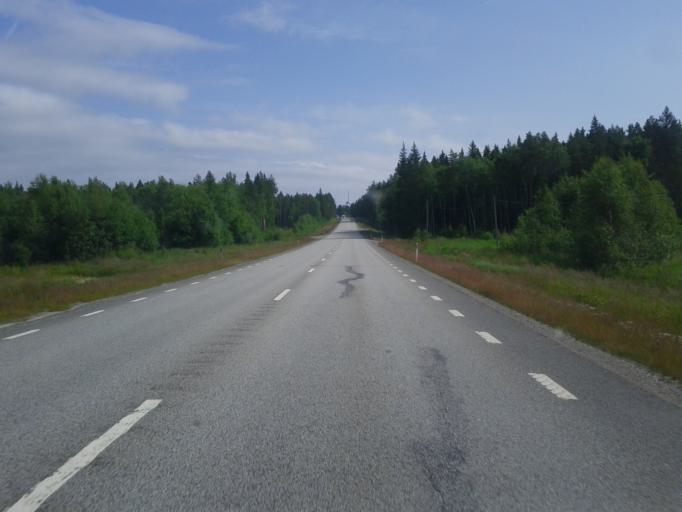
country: SE
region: Vaesterbotten
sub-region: Robertsfors Kommun
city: Robertsfors
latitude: 64.1799
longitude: 20.9716
